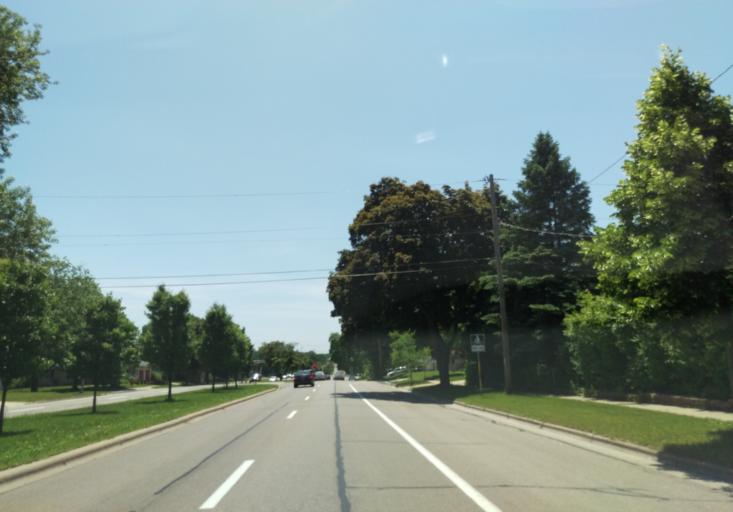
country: US
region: Wisconsin
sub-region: Dane County
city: Shorewood Hills
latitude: 43.0519
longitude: -89.4512
